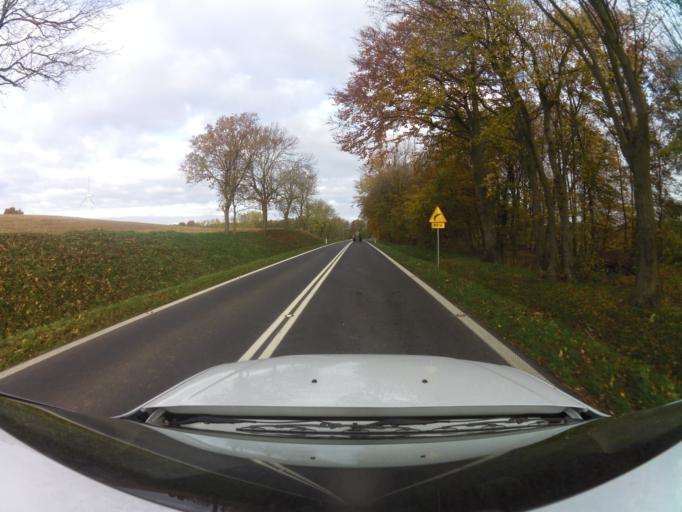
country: PL
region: West Pomeranian Voivodeship
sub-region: Powiat gryficki
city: Trzebiatow
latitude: 54.0172
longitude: 15.2423
